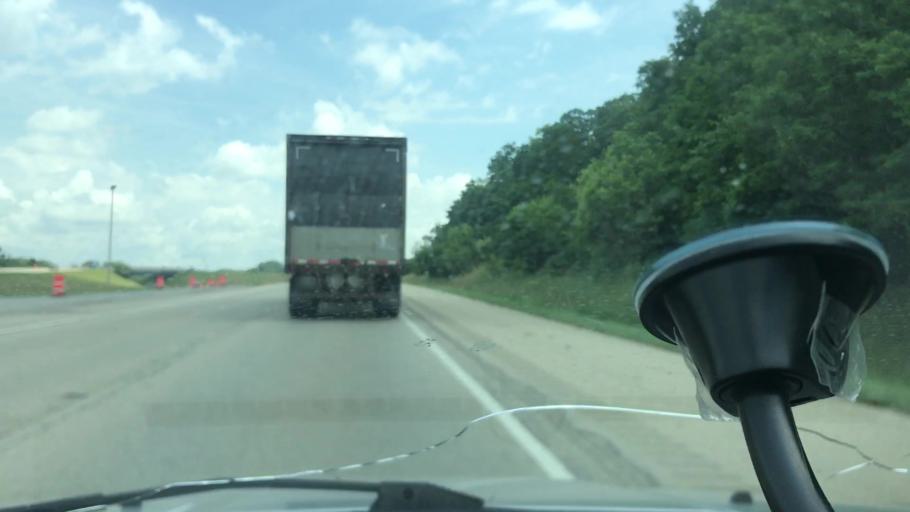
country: US
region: Illinois
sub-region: Peoria County
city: Bellevue
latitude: 40.7348
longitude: -89.6709
